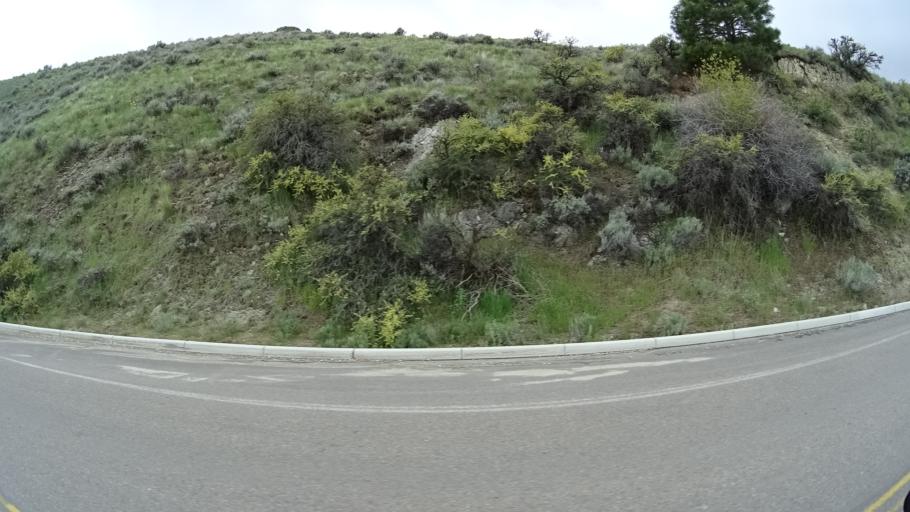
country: US
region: Idaho
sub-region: Ada County
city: Boise
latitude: 43.7201
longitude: -116.1601
